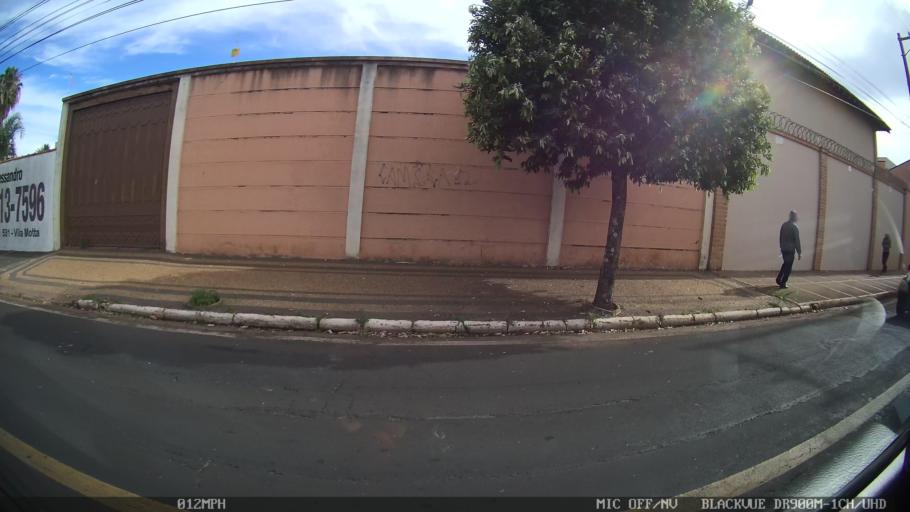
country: BR
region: Sao Paulo
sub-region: Catanduva
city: Catanduva
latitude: -21.1430
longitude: -48.9836
